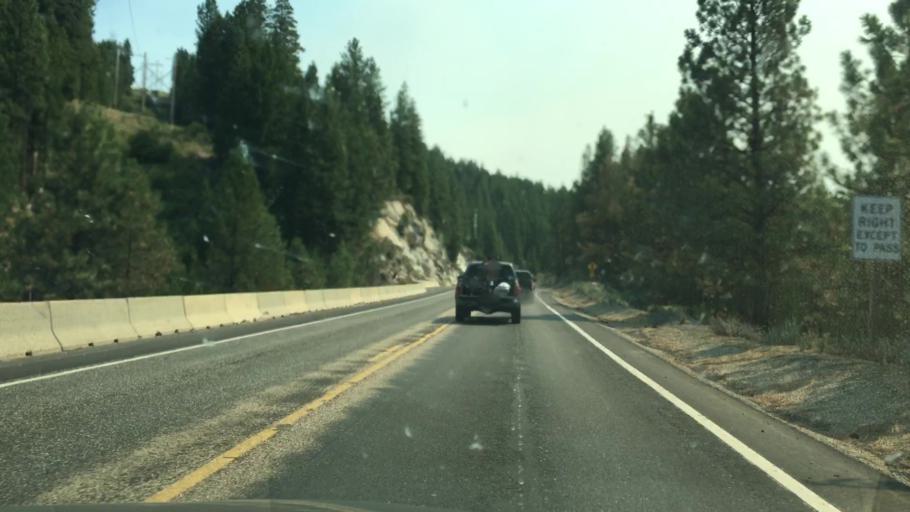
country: US
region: Idaho
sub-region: Valley County
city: Cascade
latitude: 44.5884
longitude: -116.0390
